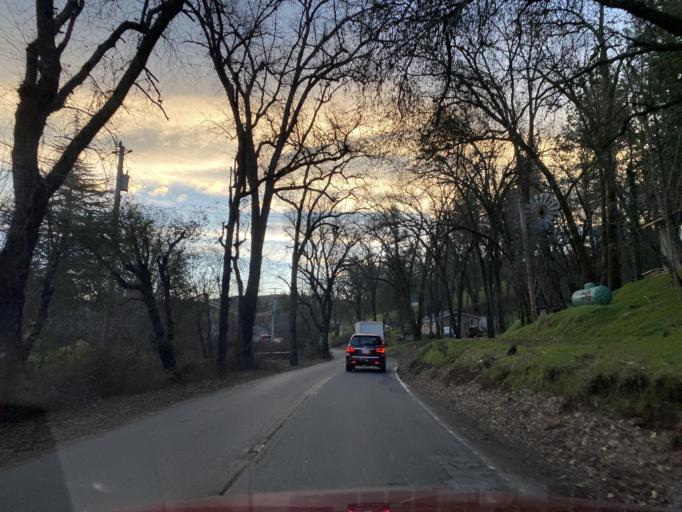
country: US
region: California
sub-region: Amador County
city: Plymouth
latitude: 38.5046
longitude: -120.7632
